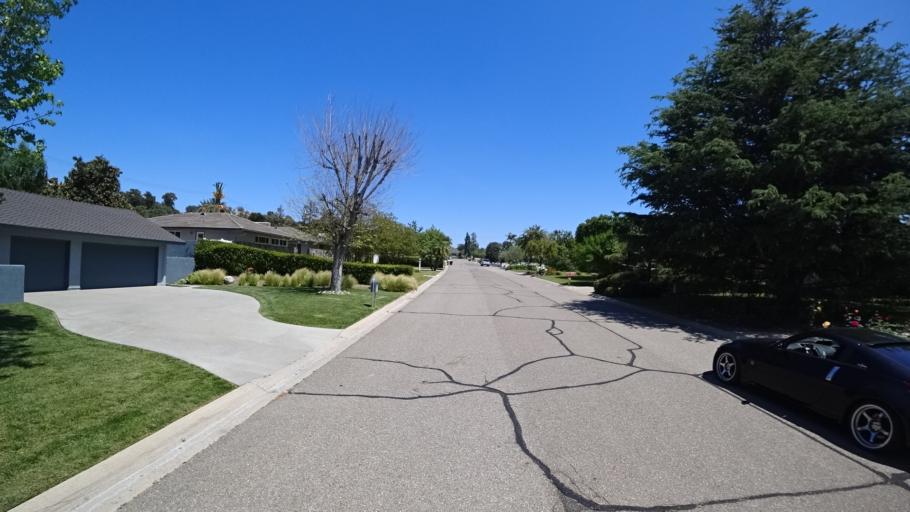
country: US
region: California
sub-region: Orange County
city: Villa Park
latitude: 33.8228
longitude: -117.8157
